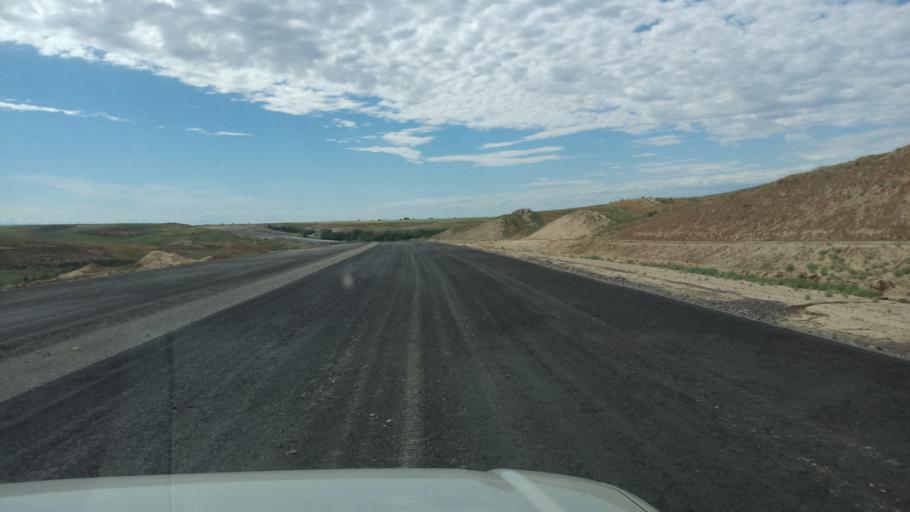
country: KG
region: Chuy
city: Bystrovka
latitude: 43.3188
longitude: 76.0711
